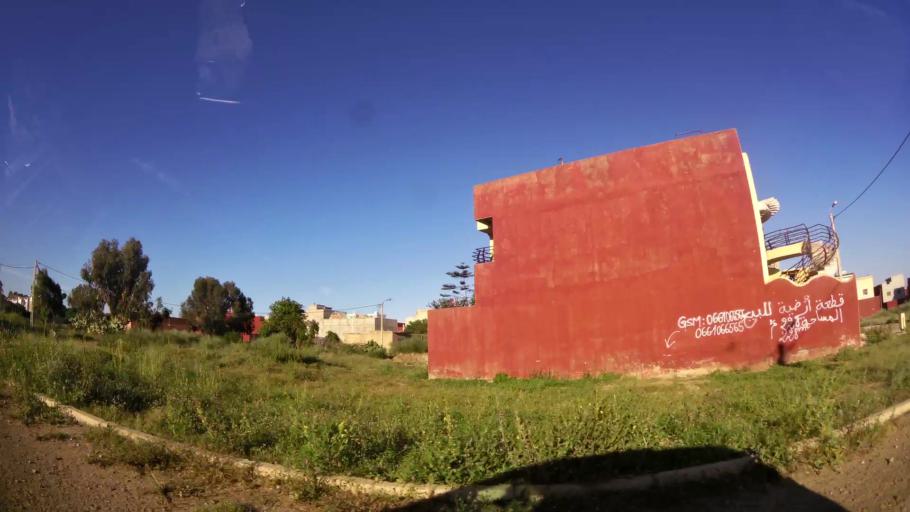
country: MA
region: Oriental
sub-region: Berkane-Taourirt
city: Madagh
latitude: 35.0848
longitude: -2.2464
